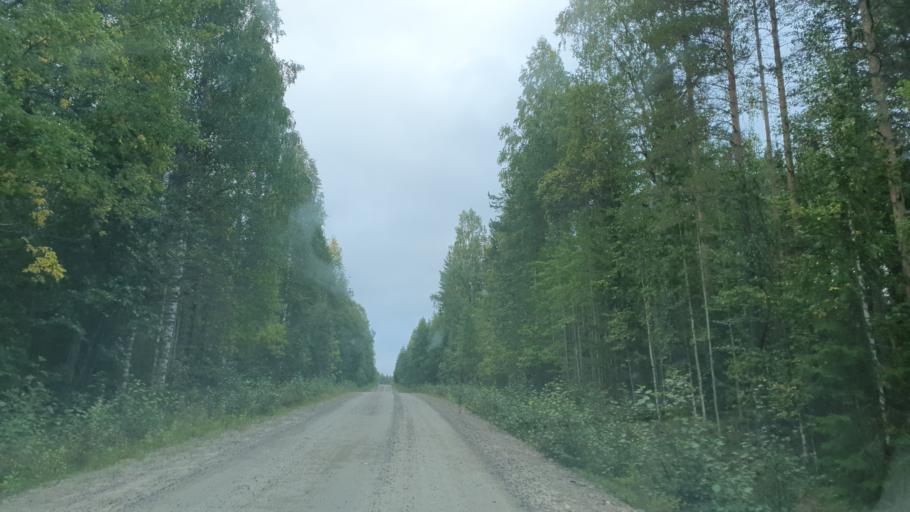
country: FI
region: Kainuu
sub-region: Kehys-Kainuu
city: Kuhmo
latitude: 64.1358
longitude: 29.5932
